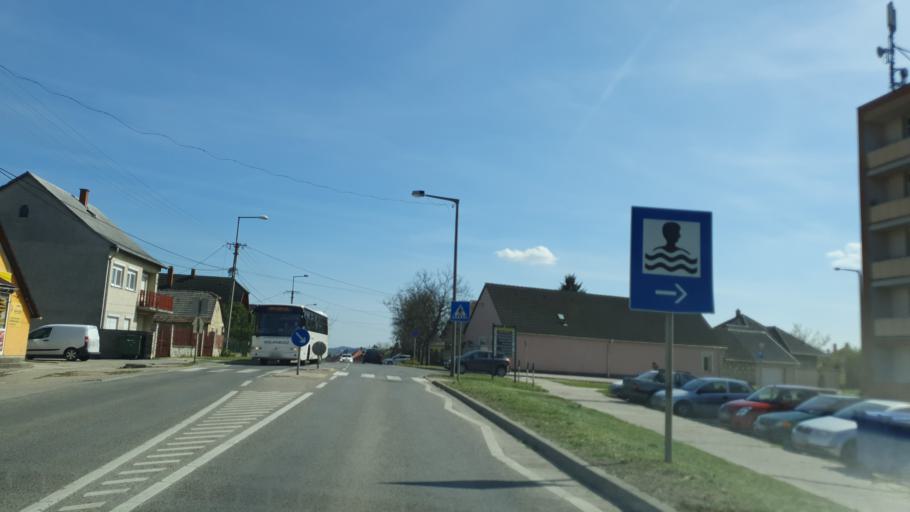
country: HU
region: Fejer
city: Mor
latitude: 47.3665
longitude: 18.2112
